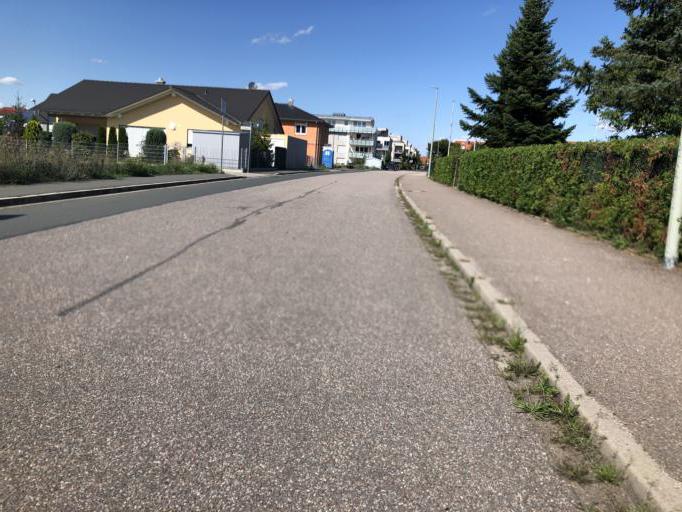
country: DE
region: Bavaria
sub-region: Regierungsbezirk Mittelfranken
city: Mohrendorf
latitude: 49.6309
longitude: 10.9910
